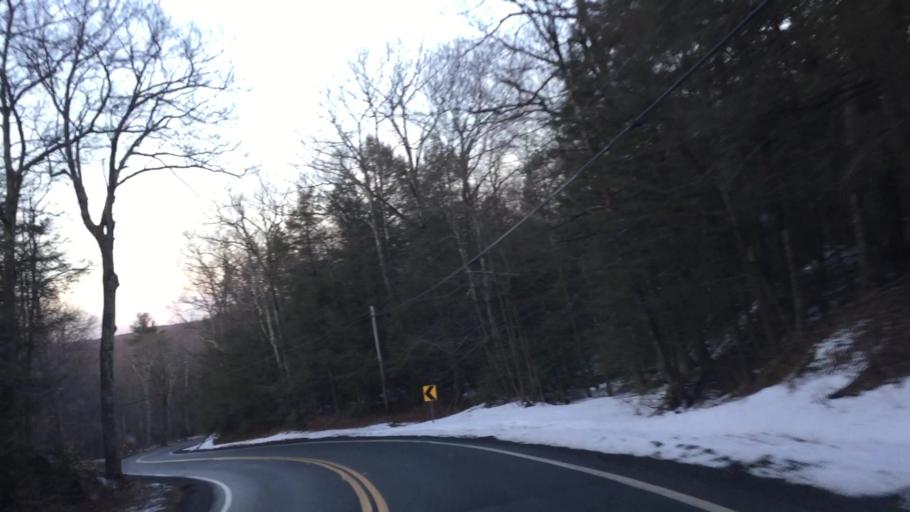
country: US
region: Massachusetts
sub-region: Berkshire County
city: Otis
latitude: 42.1720
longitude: -72.9883
